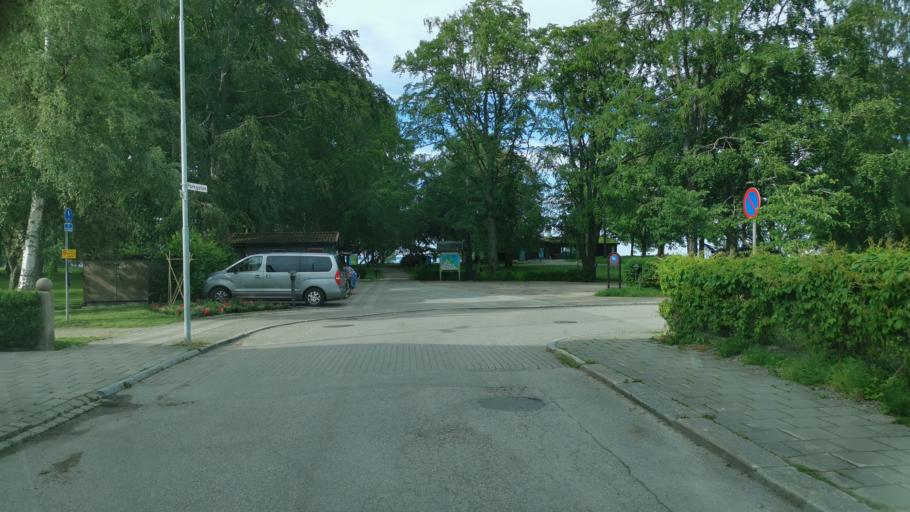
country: SE
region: Vaestra Goetaland
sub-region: Vanersborgs Kommun
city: Vanersborg
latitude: 58.3843
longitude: 12.3282
